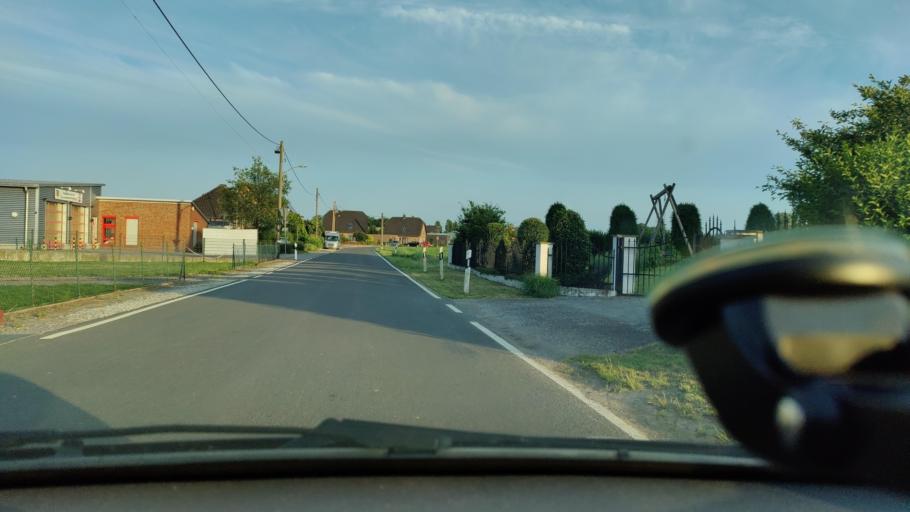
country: DE
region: North Rhine-Westphalia
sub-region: Regierungsbezirk Dusseldorf
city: Kamp-Lintfort
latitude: 51.4660
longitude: 6.5298
